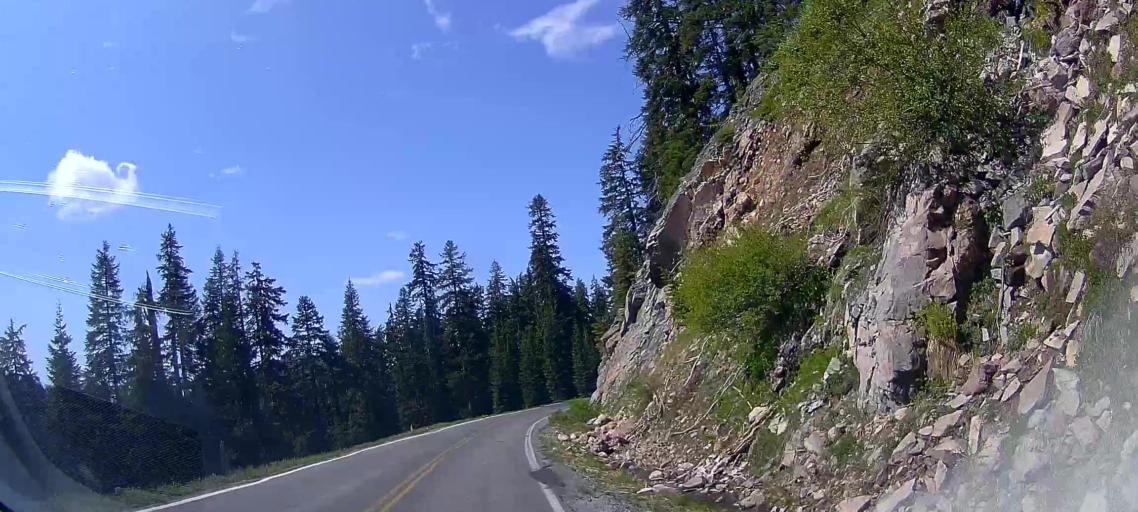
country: US
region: Oregon
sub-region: Klamath County
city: Klamath Falls
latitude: 42.8863
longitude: -122.0964
